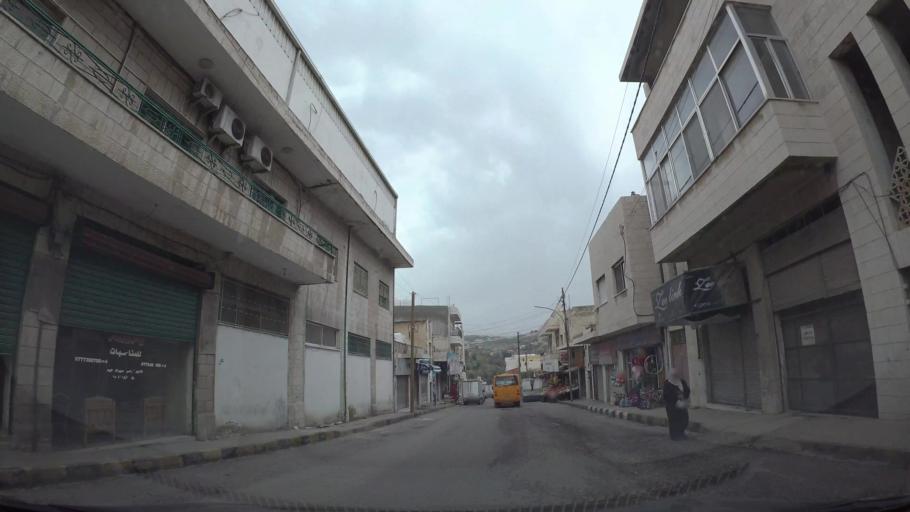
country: JO
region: Amman
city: Wadi as Sir
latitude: 31.9507
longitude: 35.8172
